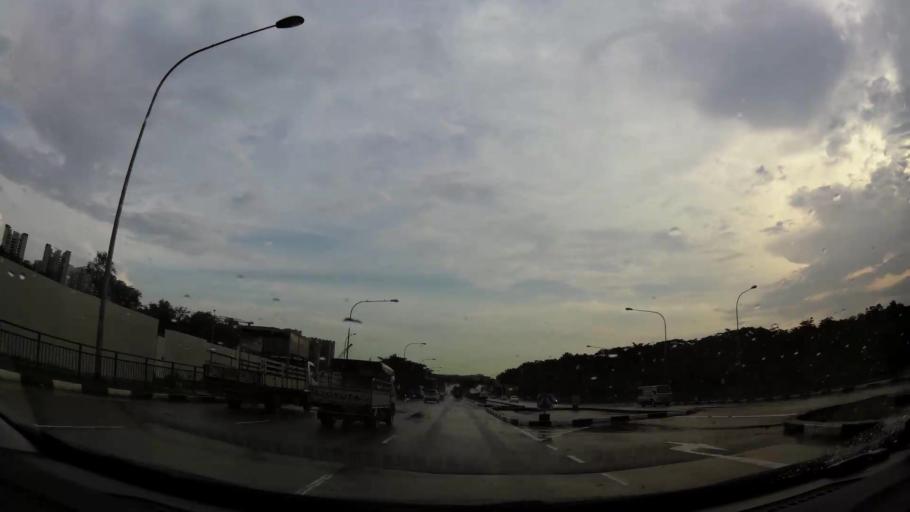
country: MY
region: Johor
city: Kampung Pasir Gudang Baru
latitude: 1.3955
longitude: 103.8691
